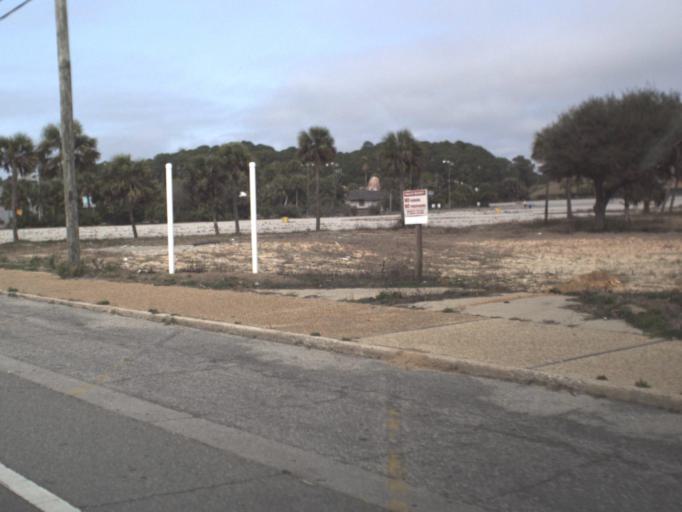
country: US
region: Florida
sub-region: Bay County
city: Panama City Beach
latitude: 30.1887
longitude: -85.8273
